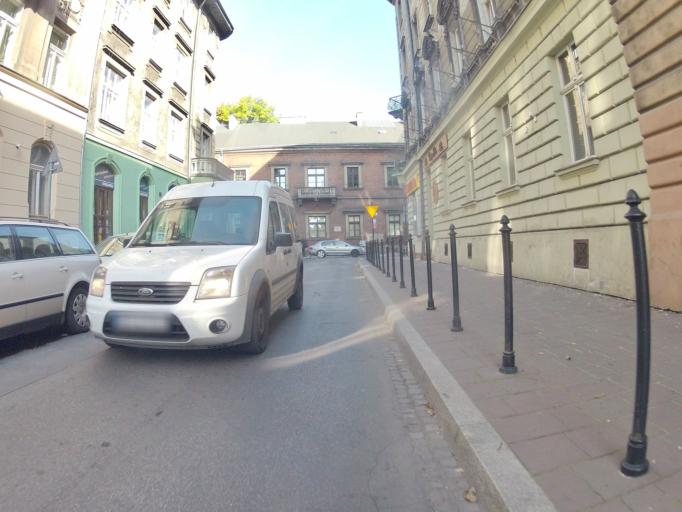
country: PL
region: Lesser Poland Voivodeship
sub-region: Krakow
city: Krakow
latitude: 50.0631
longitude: 19.9304
